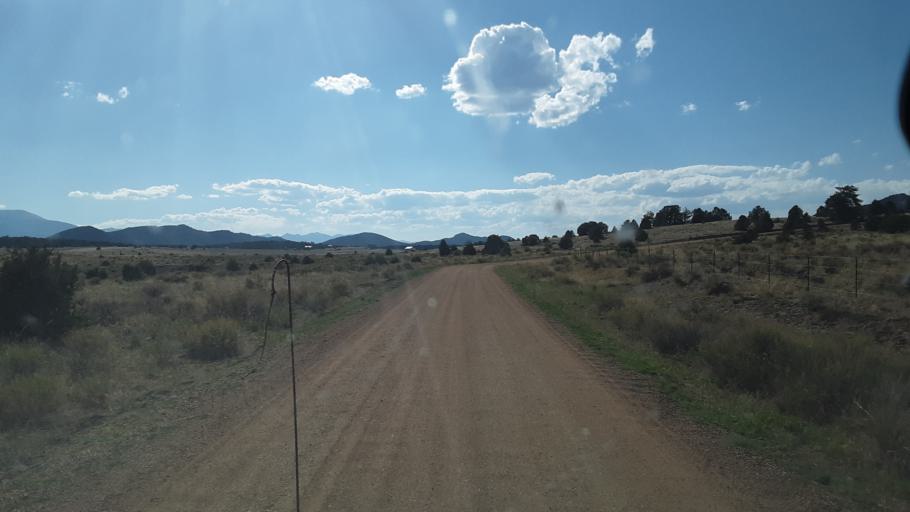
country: US
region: Colorado
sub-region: Custer County
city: Westcliffe
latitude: 38.2842
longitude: -105.4760
